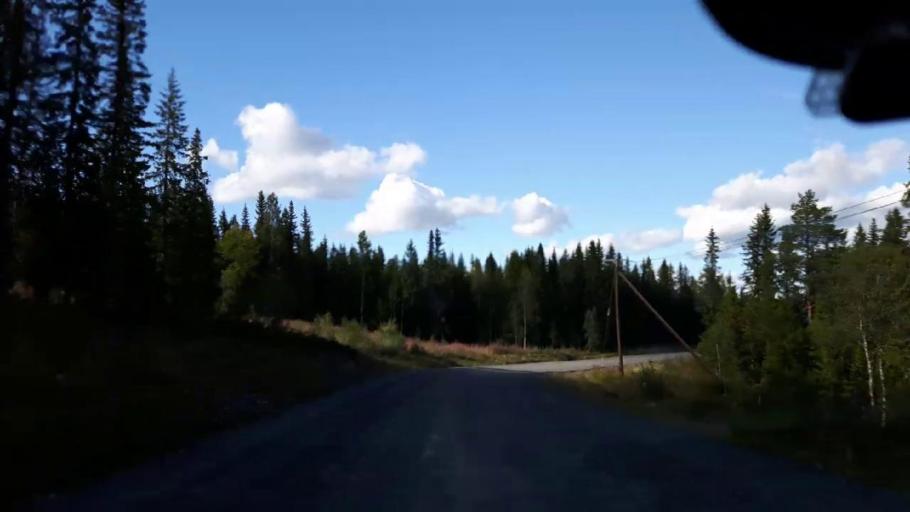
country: SE
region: Jaemtland
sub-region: Ragunda Kommun
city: Hammarstrand
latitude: 63.4313
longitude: 16.1808
